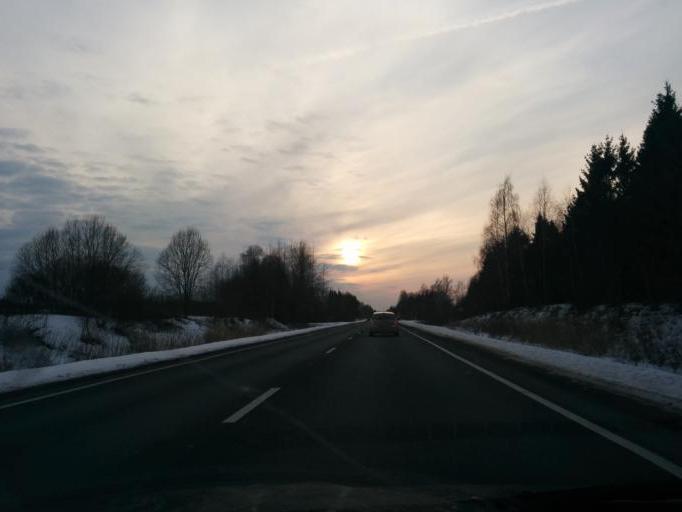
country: LV
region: Raunas
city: Rauna
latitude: 57.2876
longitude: 25.5311
